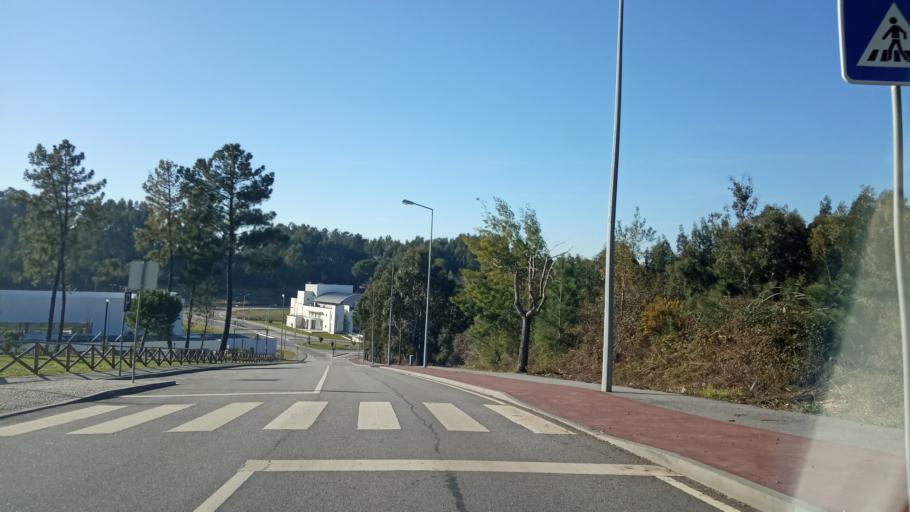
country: PT
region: Aveiro
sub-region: Anadia
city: Anadia
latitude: 40.4295
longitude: -8.4382
